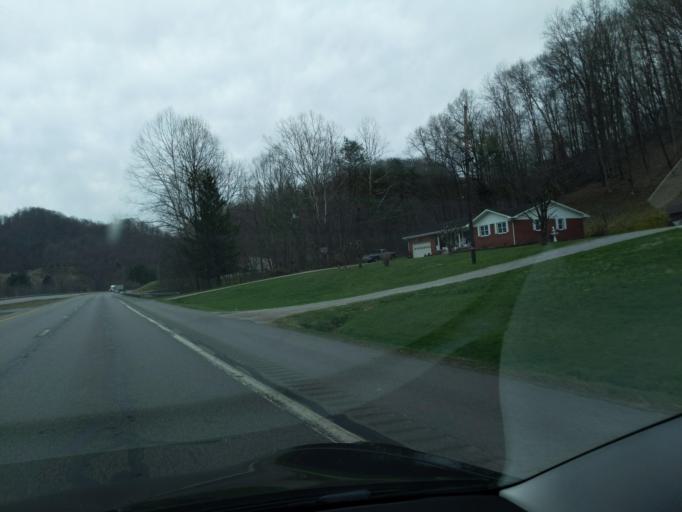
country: US
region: Kentucky
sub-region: Knox County
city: Barbourville
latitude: 36.8752
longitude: -83.8179
